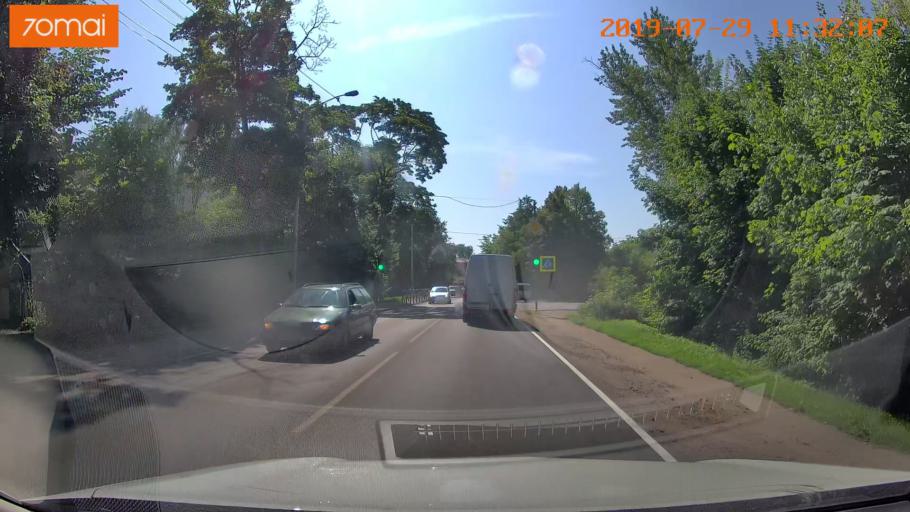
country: RU
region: Kaliningrad
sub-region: Gorod Kaliningrad
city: Kaliningrad
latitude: 54.6724
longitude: 20.5442
